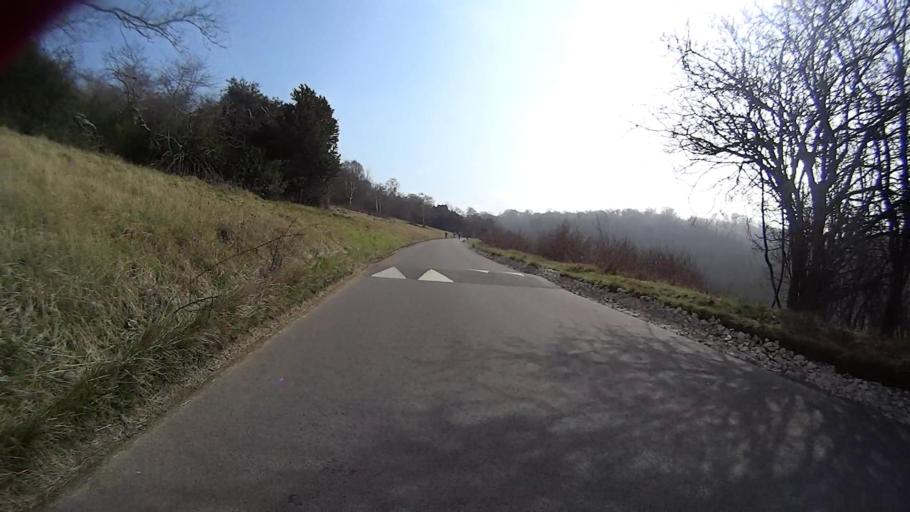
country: GB
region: England
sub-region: Surrey
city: Mickleham
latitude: 51.2546
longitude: -0.3130
